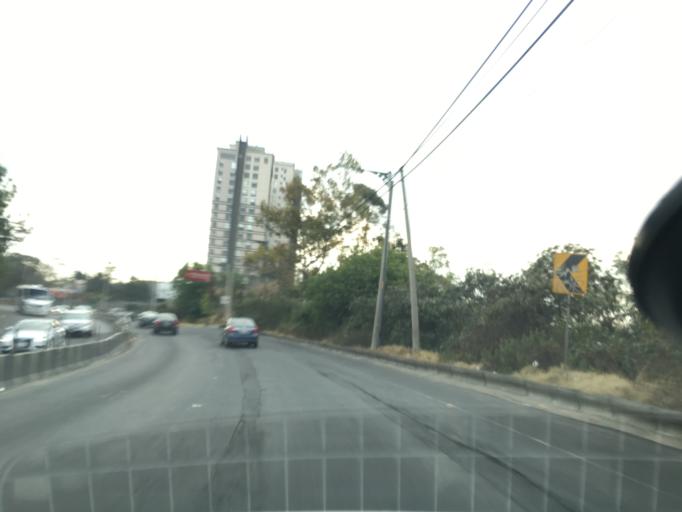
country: MX
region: Mexico City
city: Col. Bosques de las Lomas
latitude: 19.3744
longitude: -99.2667
